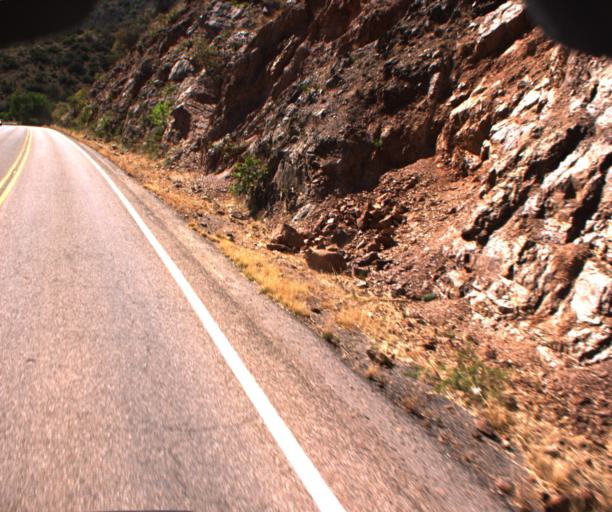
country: US
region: Arizona
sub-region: Cochise County
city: Bisbee
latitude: 31.4432
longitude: -109.9264
